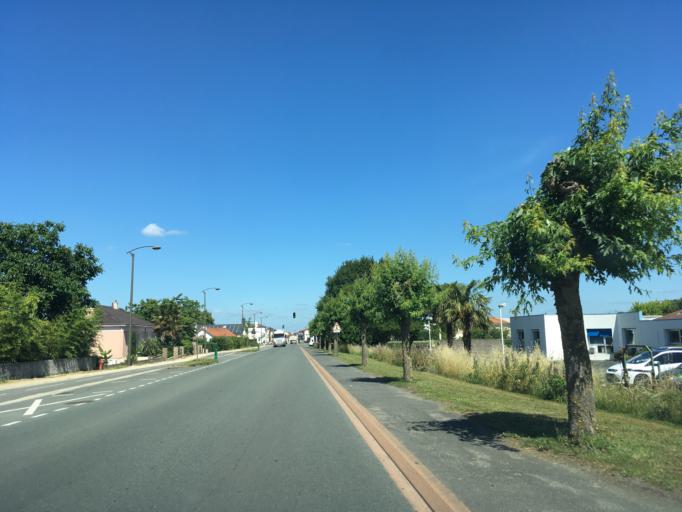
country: FR
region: Pays de la Loire
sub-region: Departement de la Vendee
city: Saint-Georges-de-Montaigu
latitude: 46.9439
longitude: -1.2888
